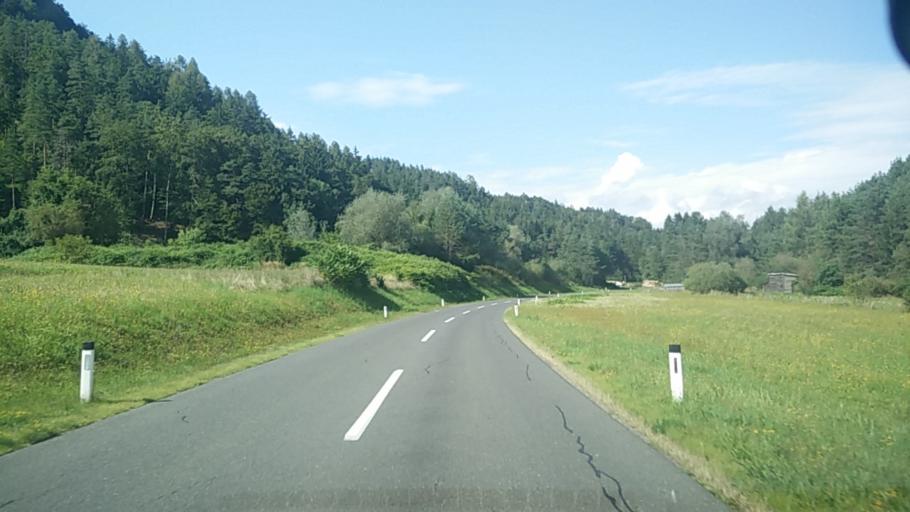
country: AT
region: Carinthia
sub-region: Politischer Bezirk Volkermarkt
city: Sittersdorf
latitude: 46.5944
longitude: 14.5667
